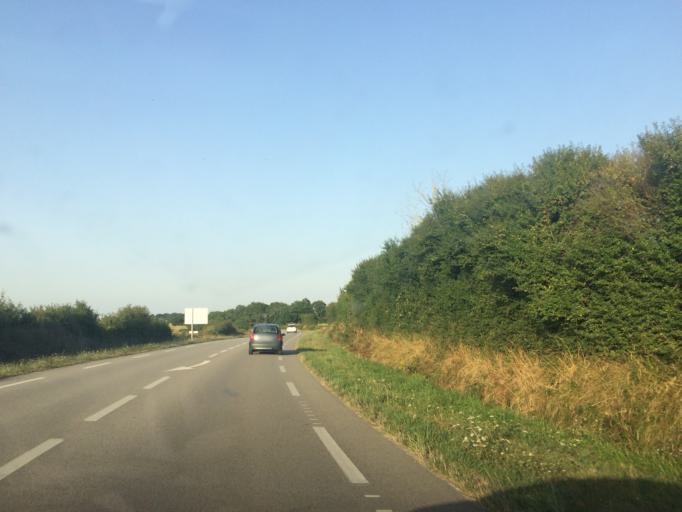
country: FR
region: Brittany
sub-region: Departement du Morbihan
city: Ambon
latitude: 47.5374
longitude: -2.5407
